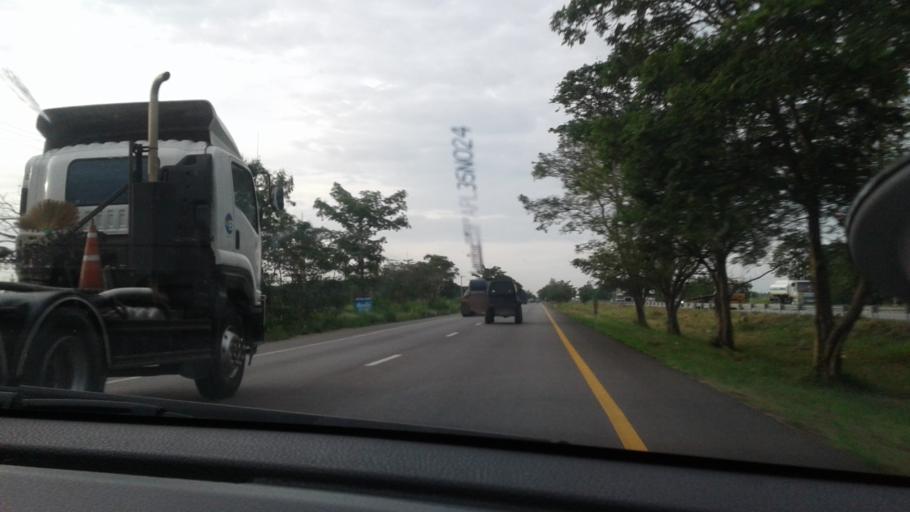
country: TH
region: Prachuap Khiri Khan
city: Pran Buri
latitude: 12.4413
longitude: 99.9092
